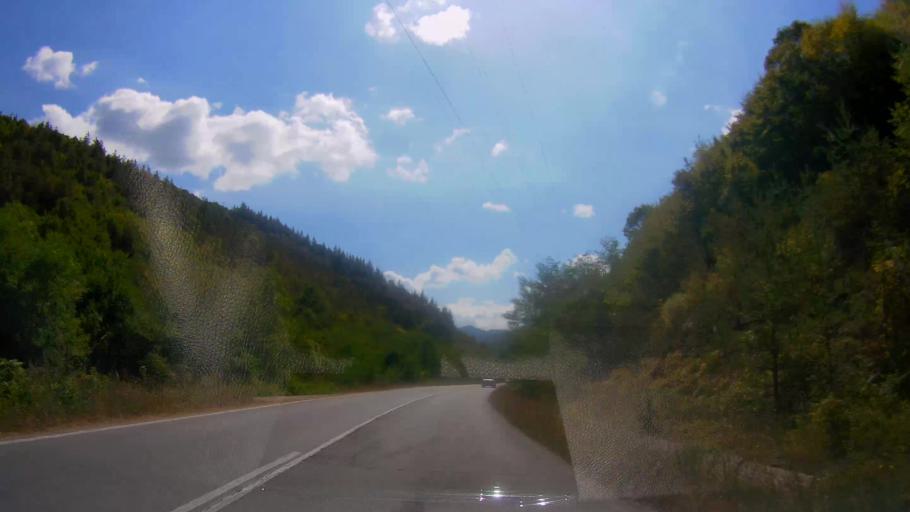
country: BG
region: Stara Zagora
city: Gurkovo
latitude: 42.7495
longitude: 25.7098
